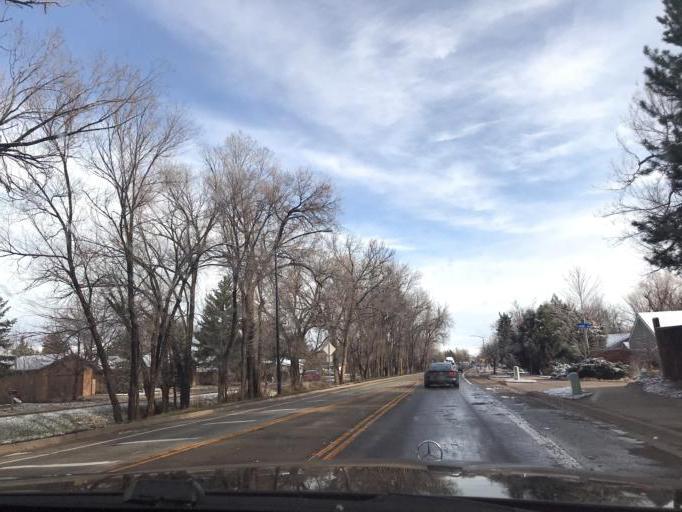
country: US
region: Colorado
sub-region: Boulder County
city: Boulder
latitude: 40.0061
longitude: -105.2253
